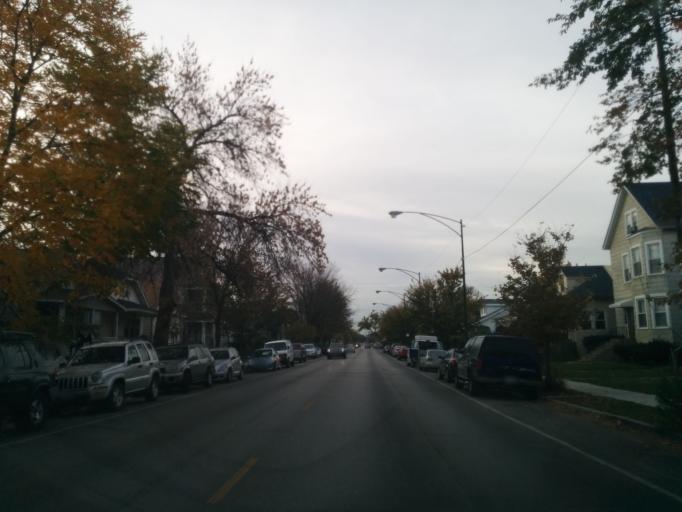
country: US
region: Illinois
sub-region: Cook County
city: Elmwood Park
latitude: 41.9215
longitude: -87.7854
